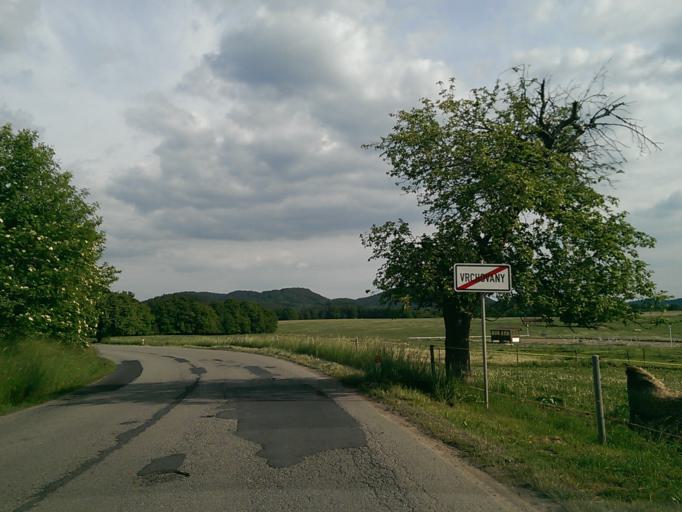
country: CZ
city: Duba
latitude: 50.5535
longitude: 14.5741
